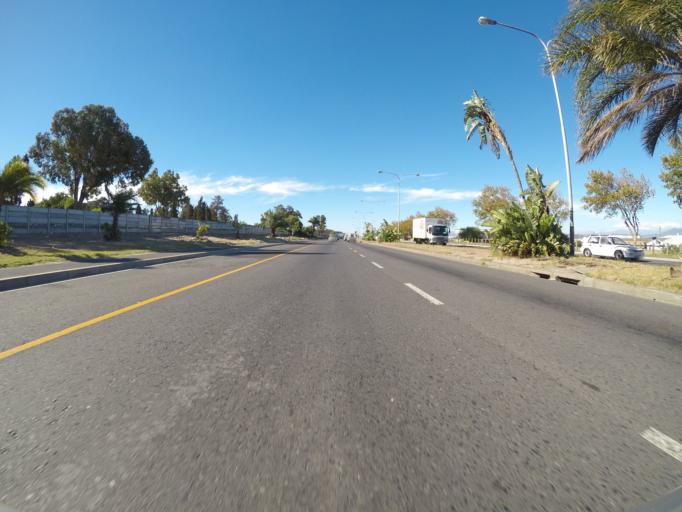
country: ZA
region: Western Cape
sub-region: City of Cape Town
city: Kraaifontein
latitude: -33.9093
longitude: 18.6660
